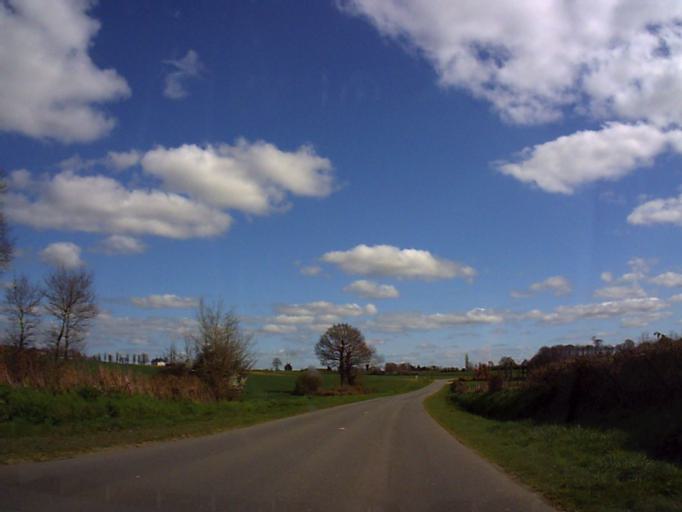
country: FR
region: Brittany
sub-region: Departement d'Ille-et-Vilaine
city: Saint-Meen-le-Grand
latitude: 48.1720
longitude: -2.1649
